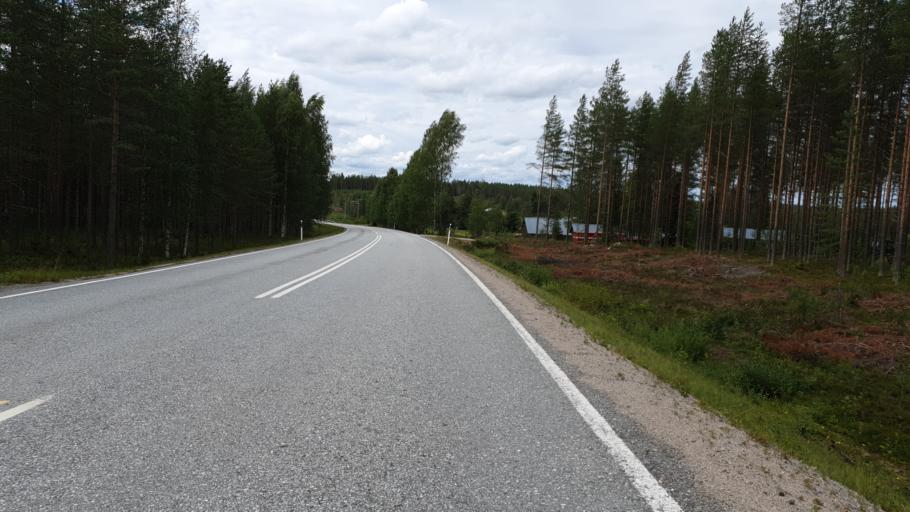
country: FI
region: Kainuu
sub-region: Kehys-Kainuu
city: Kuhmo
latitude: 64.4902
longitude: 29.8167
